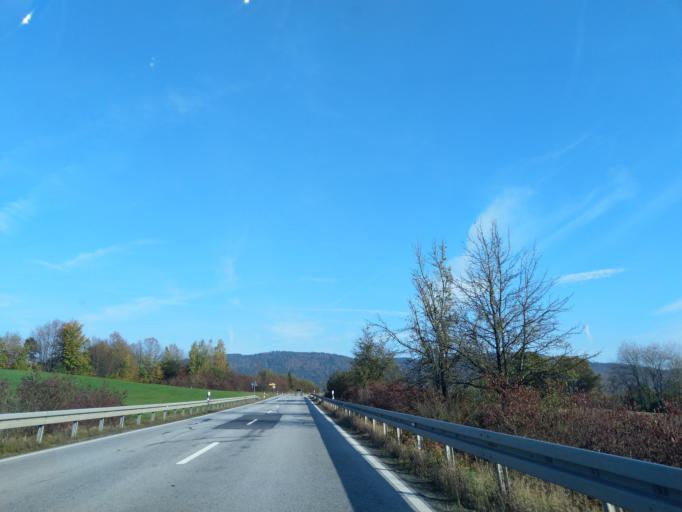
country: DE
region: Bavaria
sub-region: Lower Bavaria
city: Lalling
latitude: 48.8338
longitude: 13.1486
